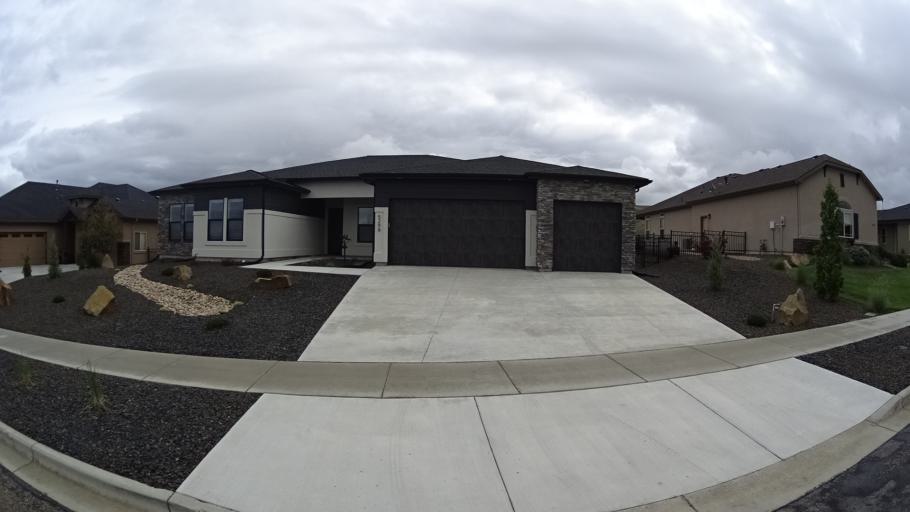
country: US
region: Idaho
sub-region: Ada County
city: Eagle
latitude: 43.7712
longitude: -116.2553
